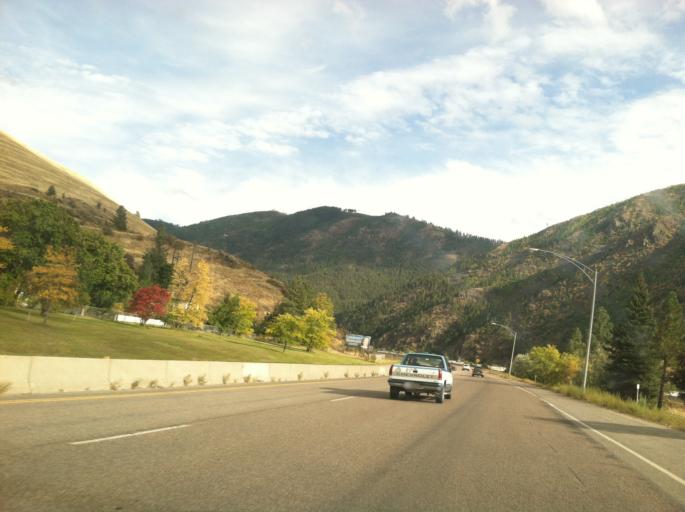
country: US
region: Montana
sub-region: Missoula County
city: Missoula
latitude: 46.8681
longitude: -113.9781
